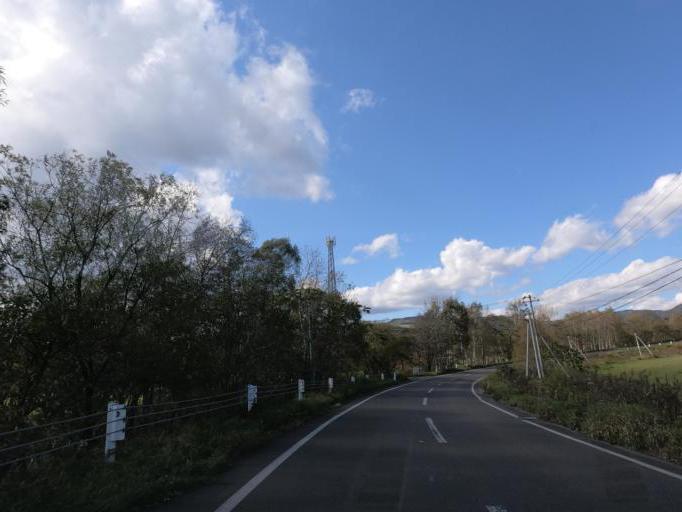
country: JP
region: Hokkaido
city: Otofuke
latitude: 43.2595
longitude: 143.2426
